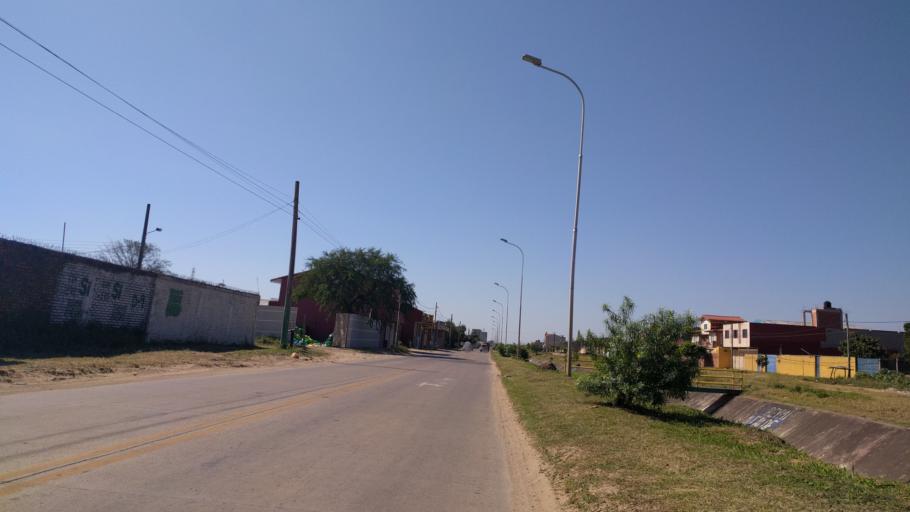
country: BO
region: Santa Cruz
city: Santa Cruz de la Sierra
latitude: -17.8431
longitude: -63.1884
